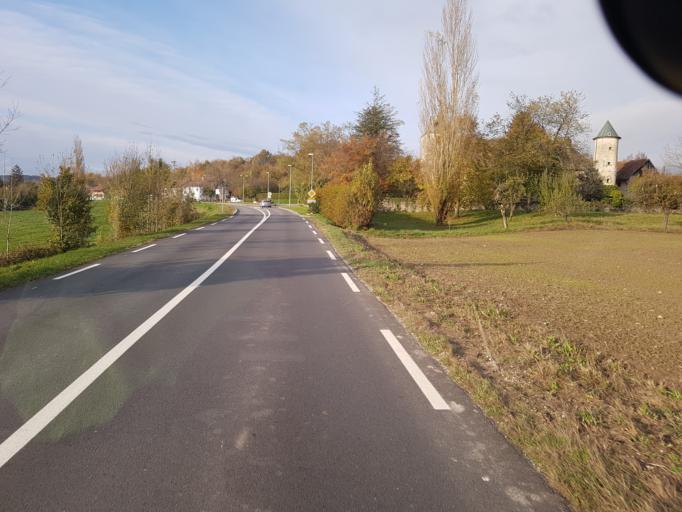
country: FR
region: Rhone-Alpes
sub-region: Departement de la Haute-Savoie
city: Frangy
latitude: 46.0398
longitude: 5.8887
